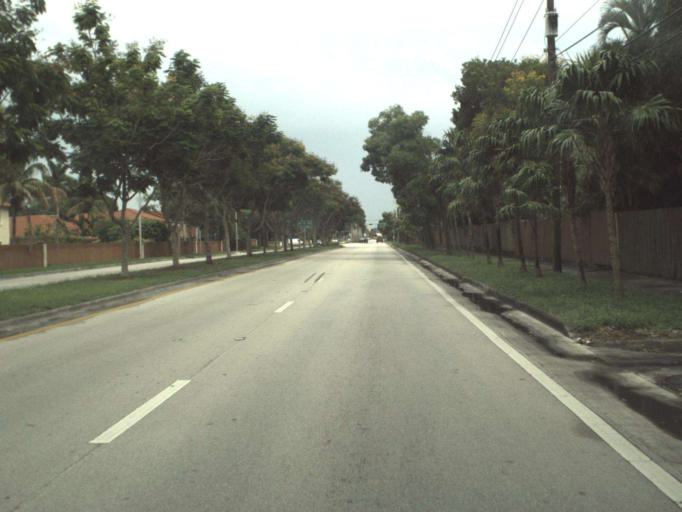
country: US
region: Florida
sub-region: Miami-Dade County
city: Palm Springs North
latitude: 25.9423
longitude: -80.3323
